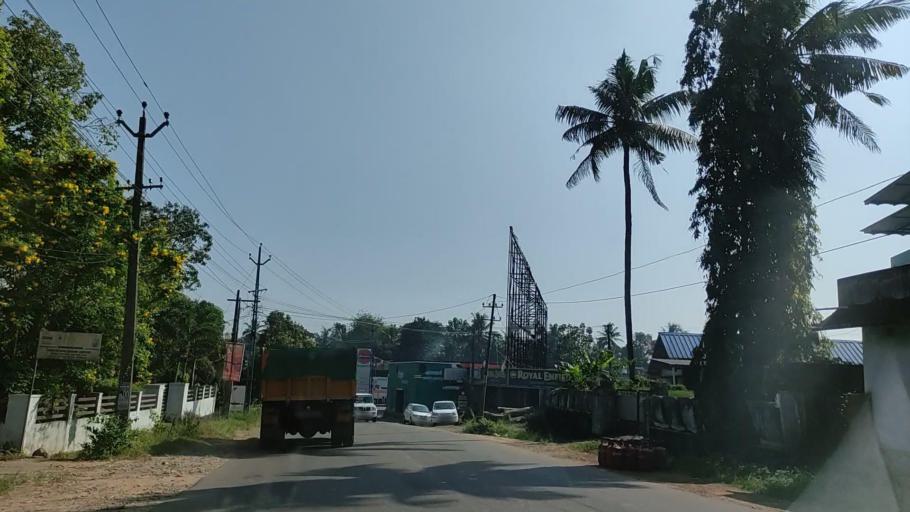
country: IN
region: Kerala
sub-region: Kollam
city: Punalur
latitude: 8.9236
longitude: 76.8992
